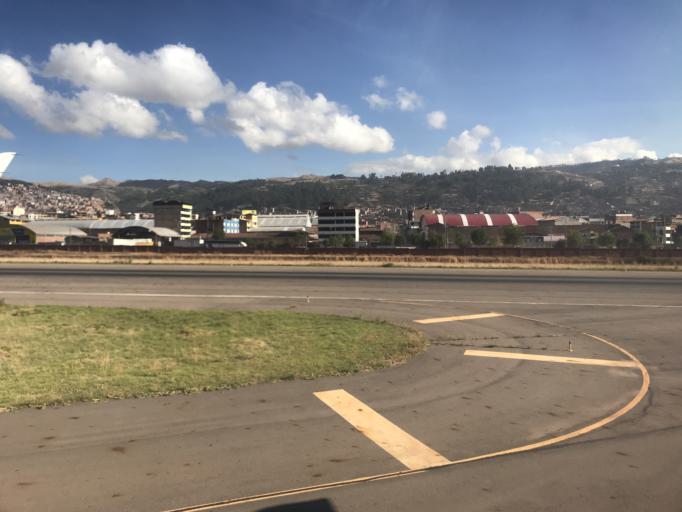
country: PE
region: Cusco
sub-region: Provincia de Cusco
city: Cusco
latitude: -13.5361
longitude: -71.9405
